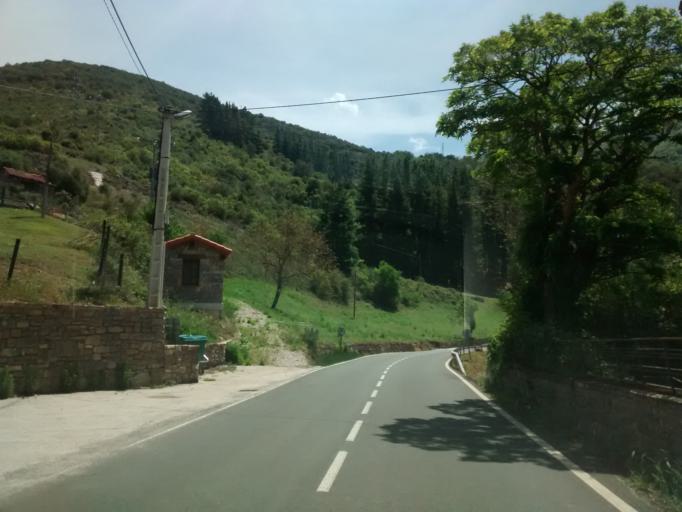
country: ES
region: Cantabria
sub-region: Provincia de Cantabria
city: Potes
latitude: 43.1212
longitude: -4.6291
